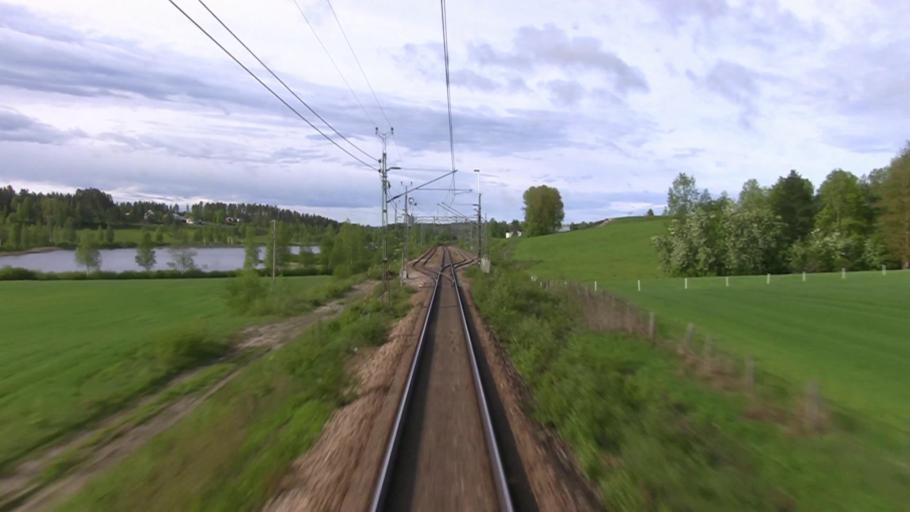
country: SE
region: Vaesterbotten
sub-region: Vindelns Kommun
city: Vindeln
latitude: 64.1030
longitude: 19.6813
